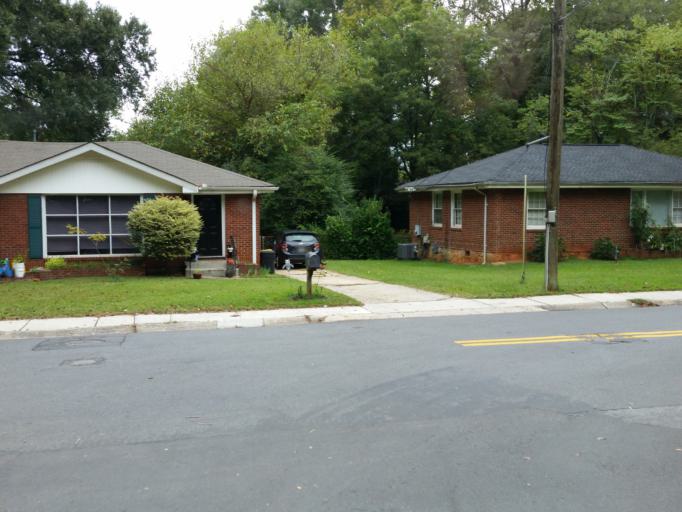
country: US
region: Georgia
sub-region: Cobb County
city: Marietta
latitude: 33.9568
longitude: -84.5321
